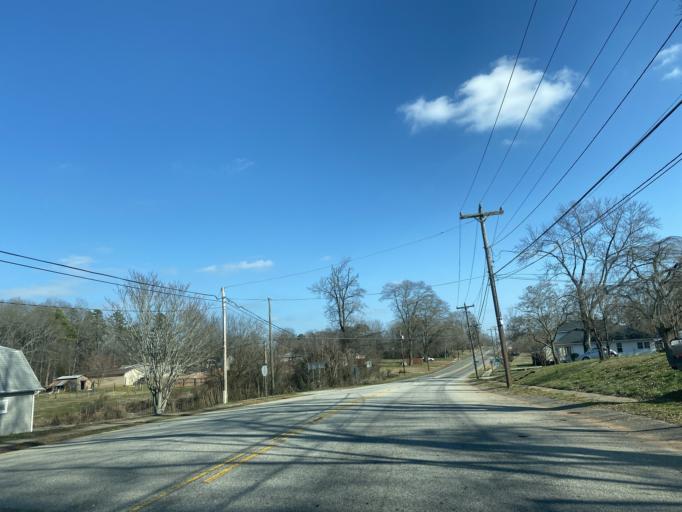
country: US
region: South Carolina
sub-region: Spartanburg County
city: Mayo
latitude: 35.1485
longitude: -81.8562
